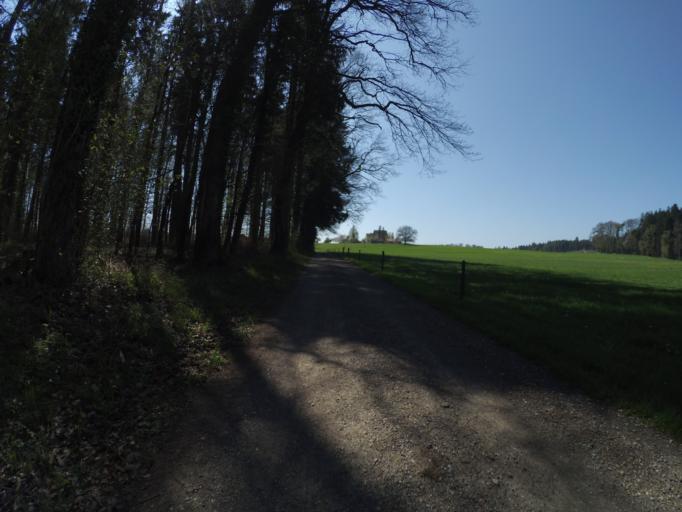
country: CH
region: Thurgau
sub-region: Frauenfeld District
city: Diessenhofen
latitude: 47.6406
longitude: 8.7409
